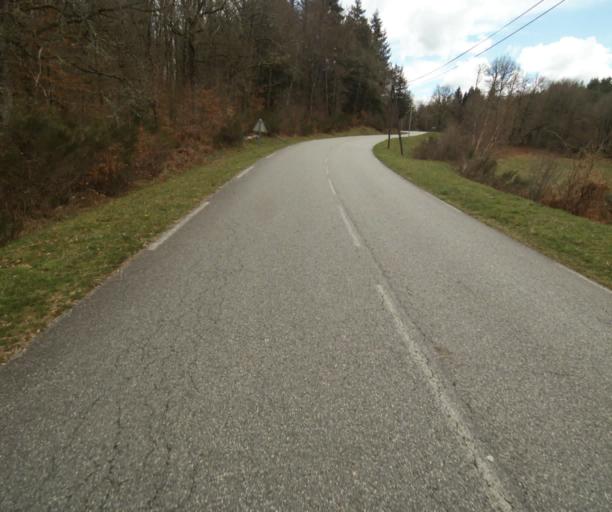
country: FR
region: Limousin
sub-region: Departement de la Correze
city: Correze
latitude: 45.3375
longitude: 1.9359
